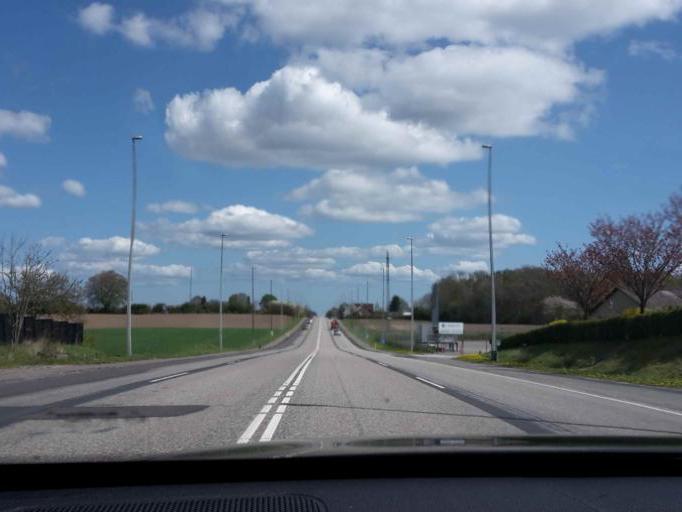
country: DK
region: South Denmark
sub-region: Odense Kommune
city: Bellinge
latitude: 55.3914
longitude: 10.2917
